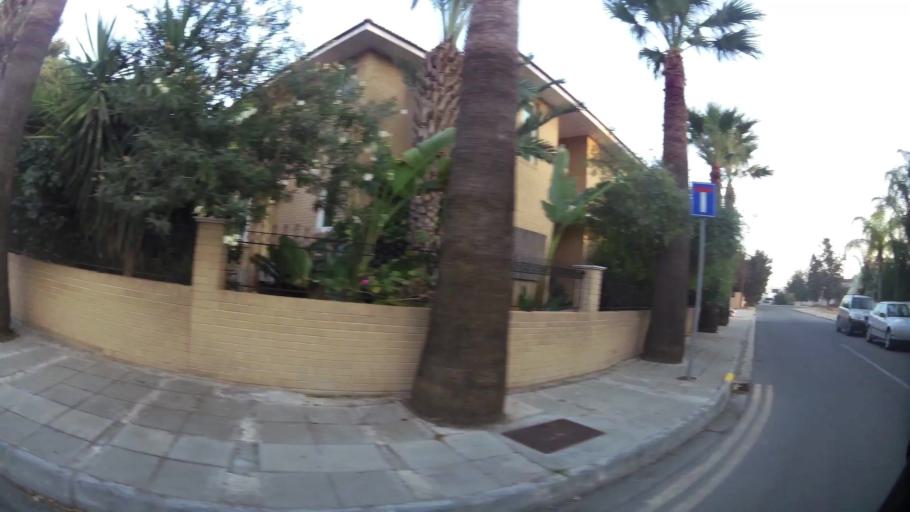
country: CY
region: Lefkosia
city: Nicosia
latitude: 35.1615
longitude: 33.3289
